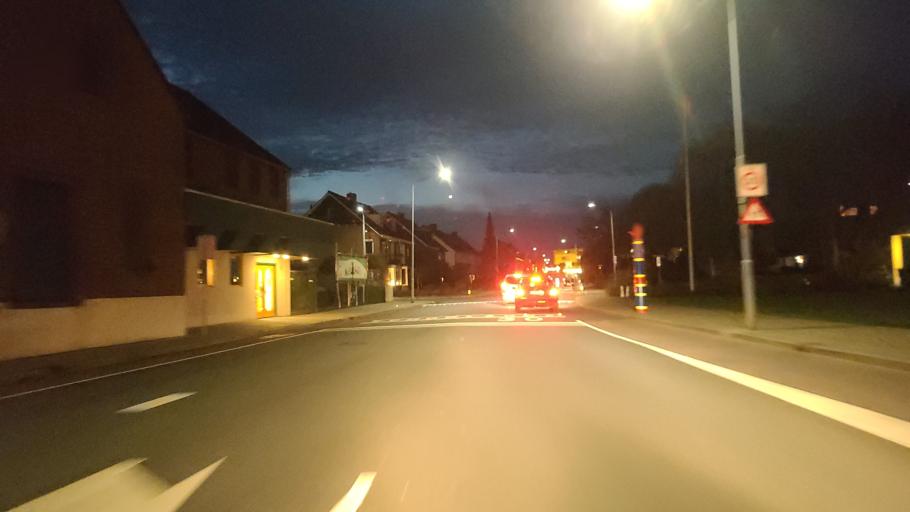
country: NL
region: Limburg
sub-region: Gemeente Venlo
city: Venlo
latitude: 51.3755
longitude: 6.1825
